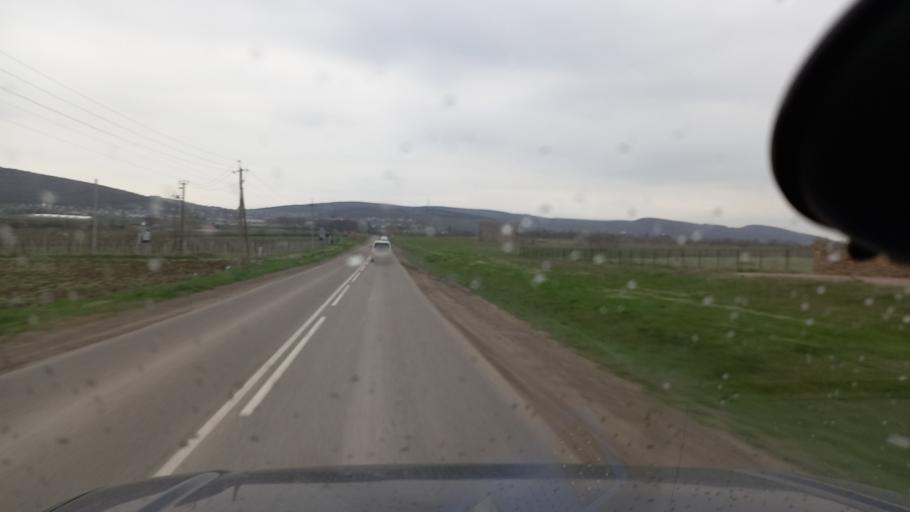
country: RU
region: Krasnodarskiy
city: Anapskaya
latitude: 44.8770
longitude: 37.4485
